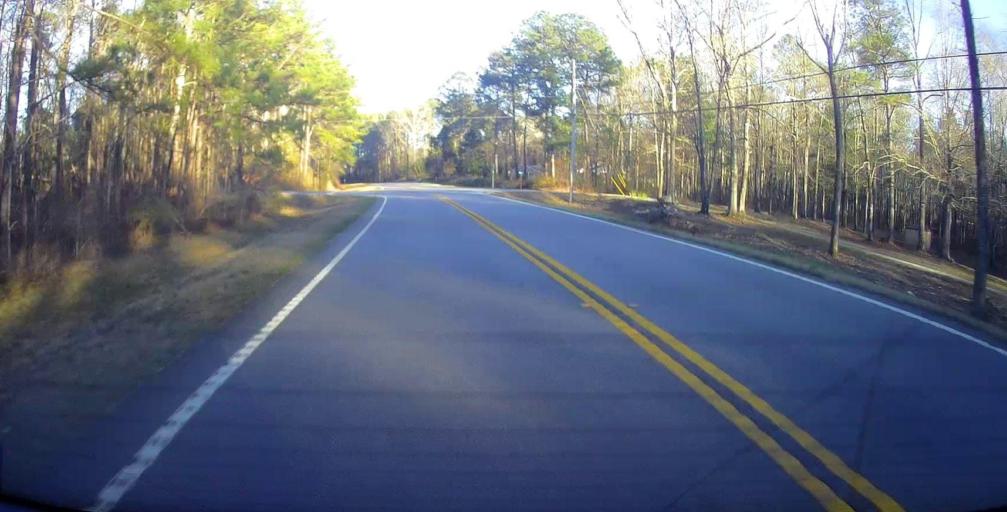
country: US
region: Georgia
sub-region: Harris County
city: Hamilton
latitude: 32.6273
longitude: -84.7880
